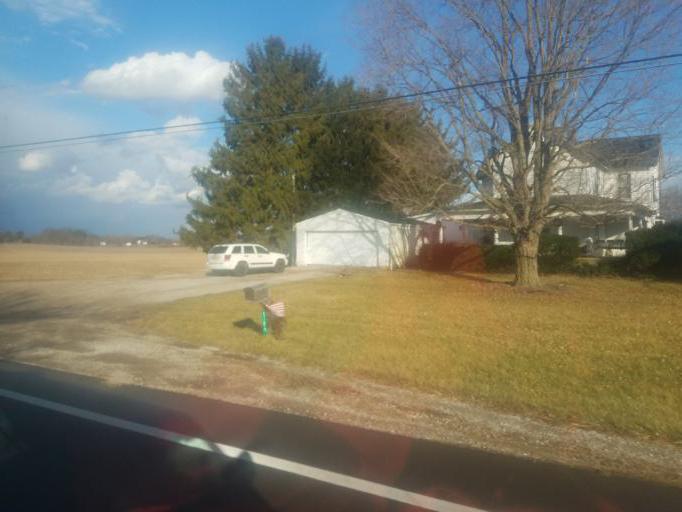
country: US
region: Ohio
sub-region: Delaware County
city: Delaware
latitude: 40.3425
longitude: -83.1361
